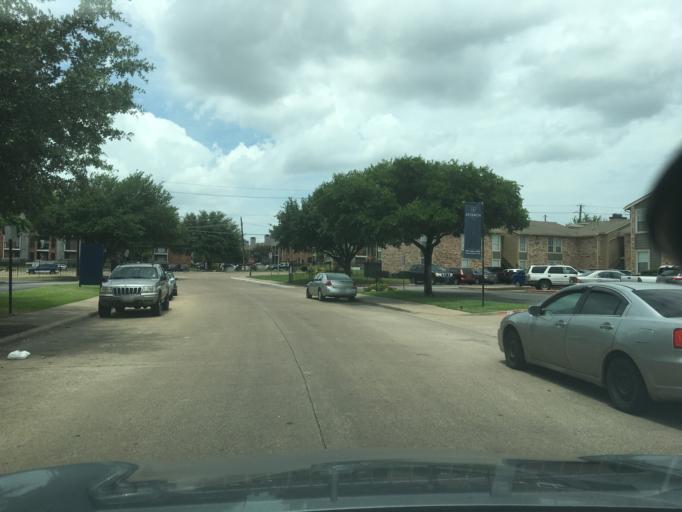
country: US
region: Texas
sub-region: Dallas County
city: Richardson
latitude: 32.9245
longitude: -96.7171
